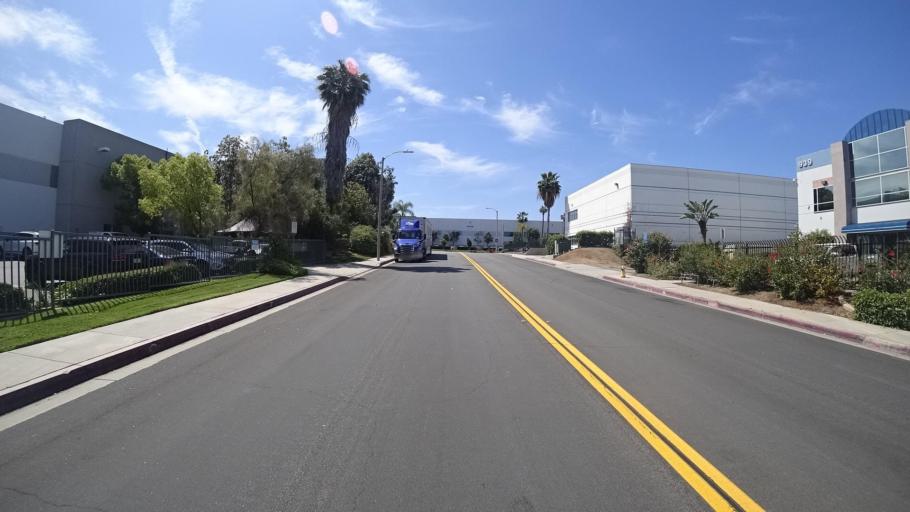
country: US
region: California
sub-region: Los Angeles County
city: South San Jose Hills
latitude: 34.0025
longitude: -117.9182
